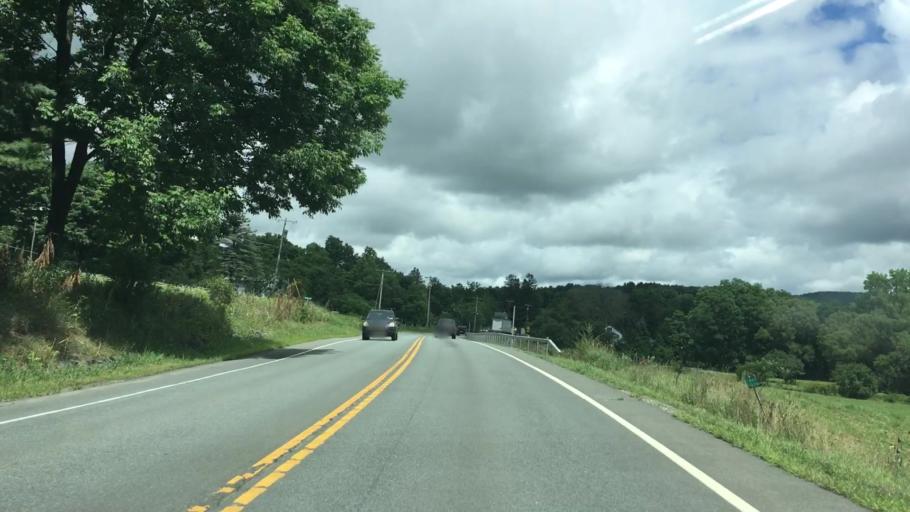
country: US
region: New York
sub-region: Rensselaer County
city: Hoosick Falls
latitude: 42.8751
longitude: -73.3049
